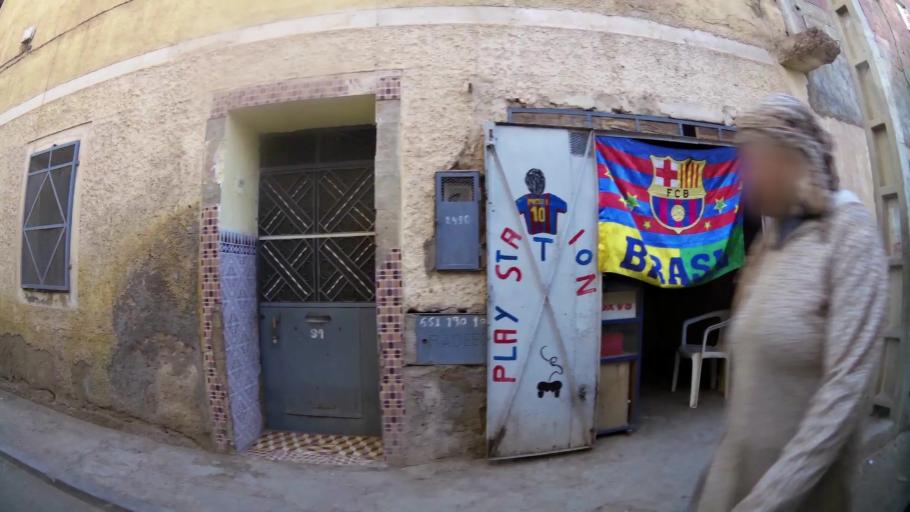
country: MA
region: Oriental
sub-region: Oujda-Angad
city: Oujda
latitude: 34.7131
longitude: -1.8902
